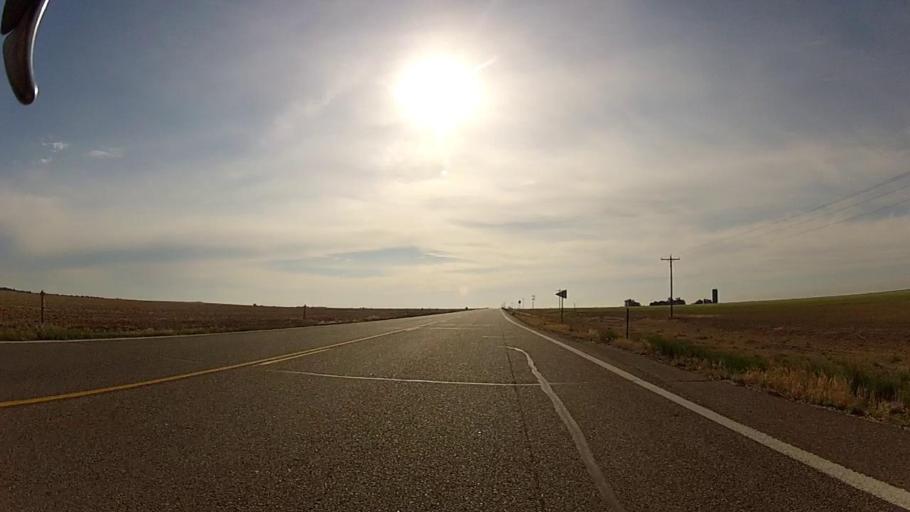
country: US
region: Kansas
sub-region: Grant County
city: Ulysses
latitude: 37.5766
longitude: -101.4519
